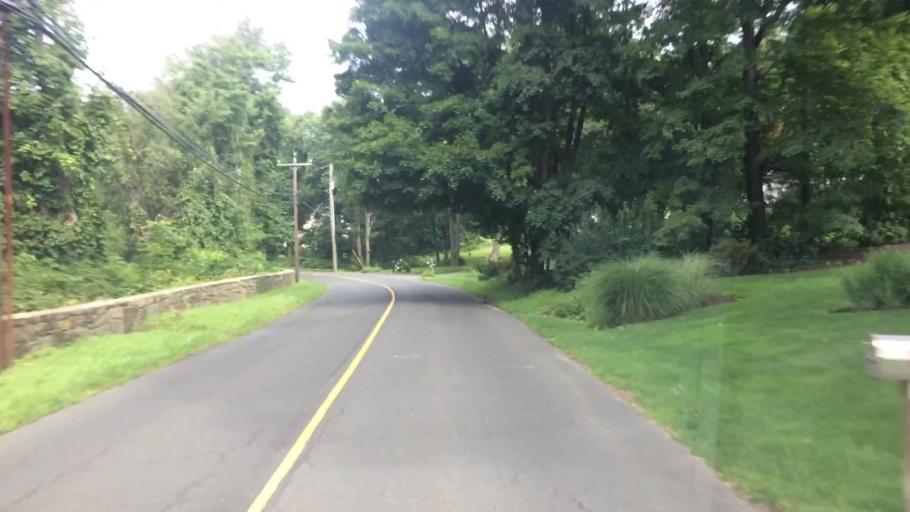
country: US
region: Connecticut
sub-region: Fairfield County
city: Danbury
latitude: 41.4123
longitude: -73.5085
